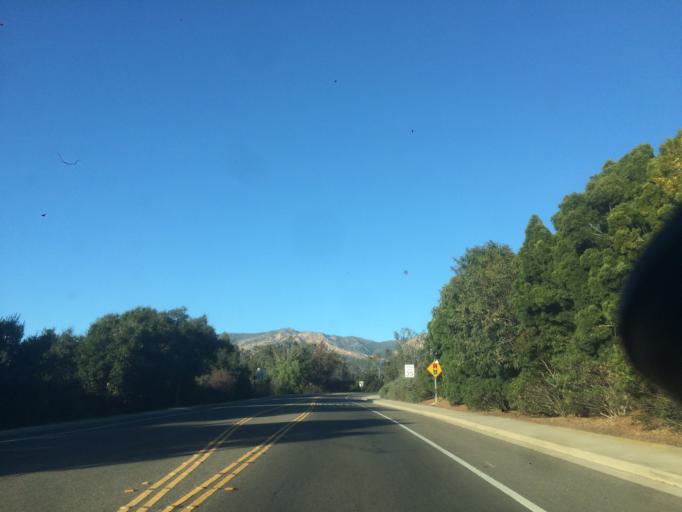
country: US
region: California
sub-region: Santa Barbara County
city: Mission Canyon
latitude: 34.4239
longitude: -119.7372
